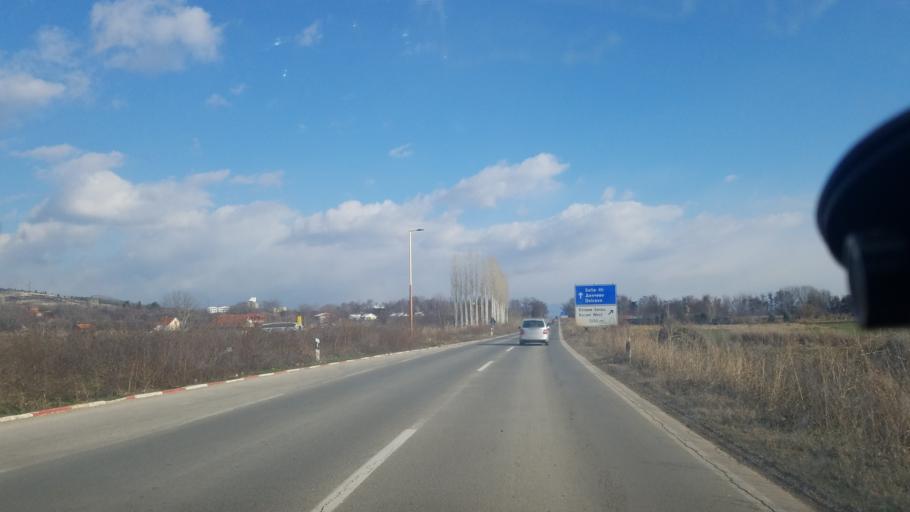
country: MK
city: Obleshevo
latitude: 41.8993
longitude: 22.3724
